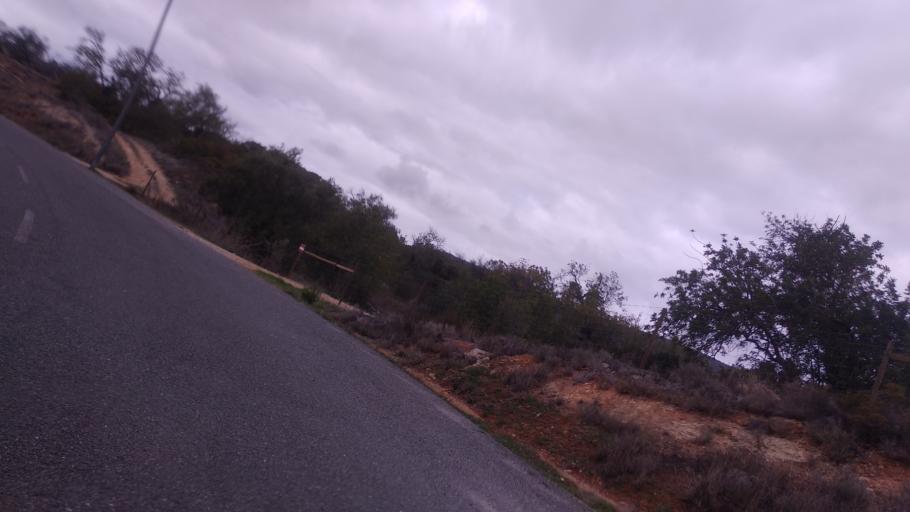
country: PT
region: Faro
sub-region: Faro
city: Santa Barbara de Nexe
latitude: 37.0908
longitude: -7.9754
